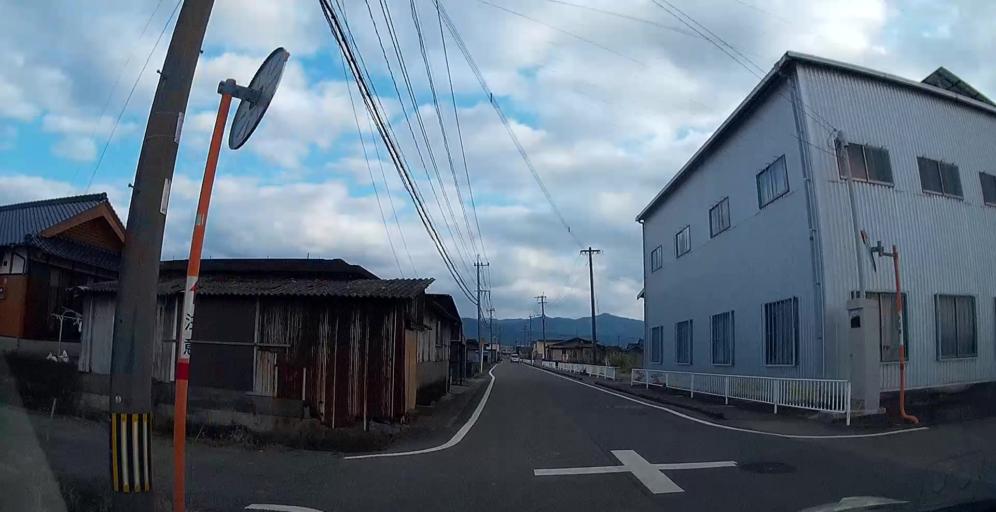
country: JP
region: Kumamoto
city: Yatsushiro
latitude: 32.5434
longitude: 130.6214
